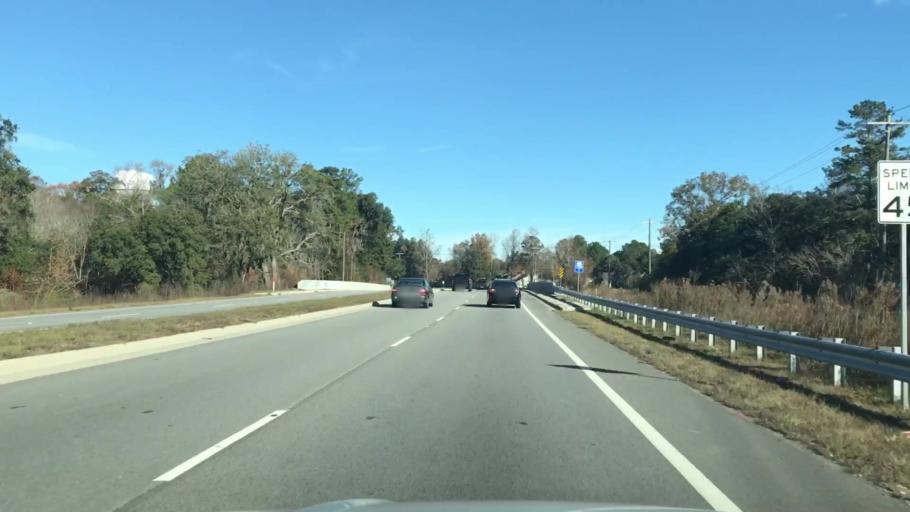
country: US
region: South Carolina
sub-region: Dorchester County
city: Centerville
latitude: 32.9573
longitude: -80.2010
